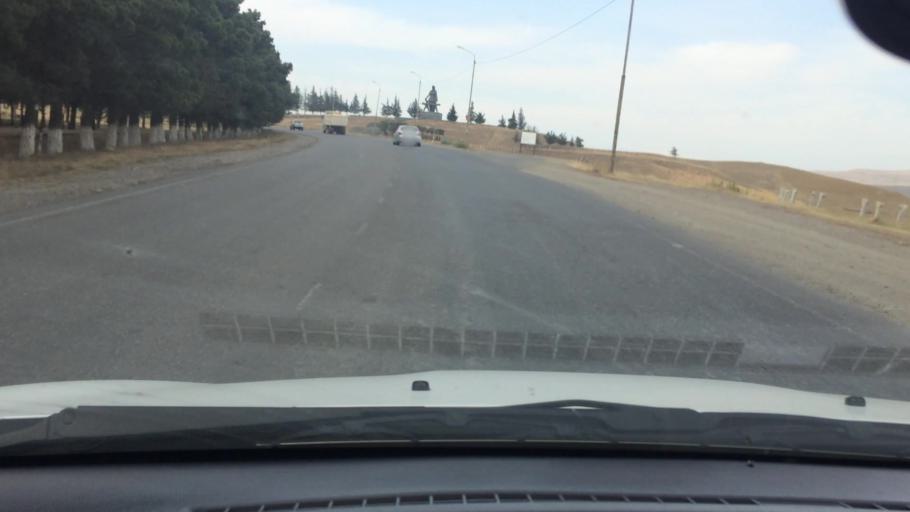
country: GE
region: Kvemo Kartli
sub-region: Marneuli
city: Marneuli
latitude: 41.4995
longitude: 44.8034
